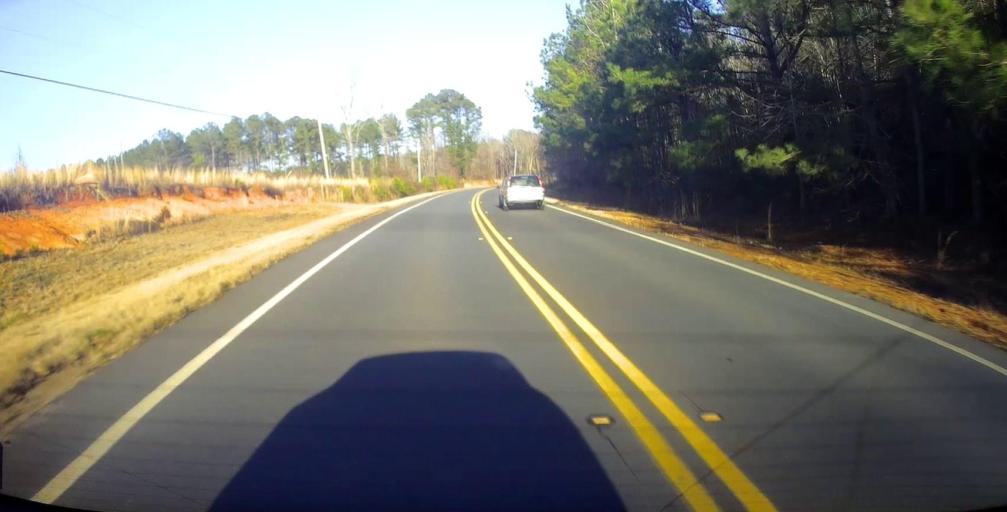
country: US
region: Georgia
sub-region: Harris County
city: Pine Mountain
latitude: 32.9157
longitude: -84.7979
